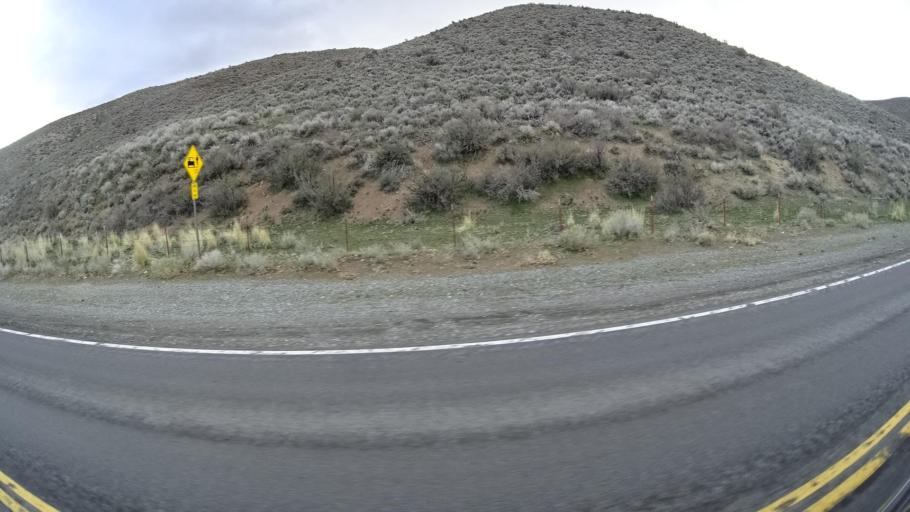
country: US
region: Nevada
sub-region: Carson City
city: Carson City
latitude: 39.2175
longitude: -119.8017
